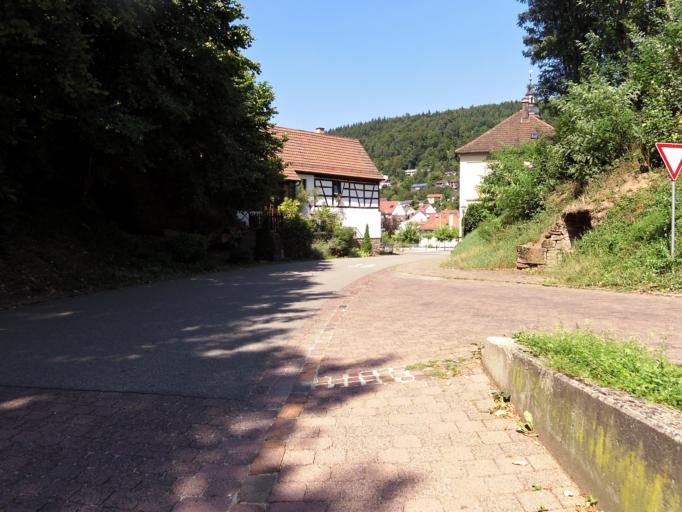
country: DE
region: Baden-Wuerttemberg
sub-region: Karlsruhe Region
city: Neckargerach
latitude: 49.3988
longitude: 9.0709
